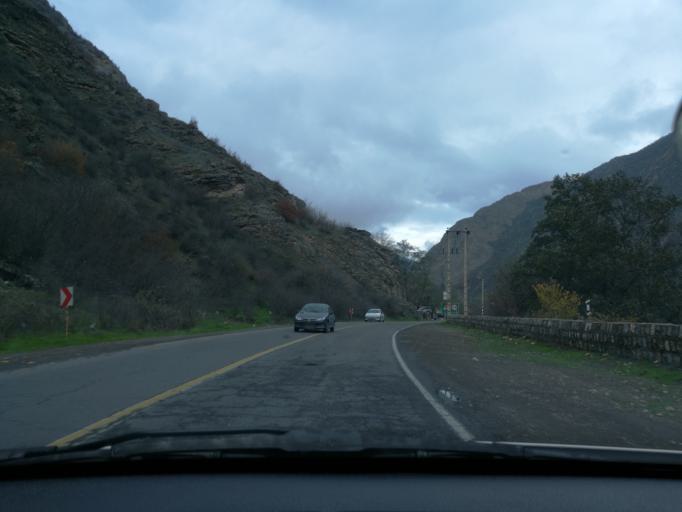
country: IR
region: Mazandaran
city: Chalus
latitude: 36.3544
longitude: 51.2613
